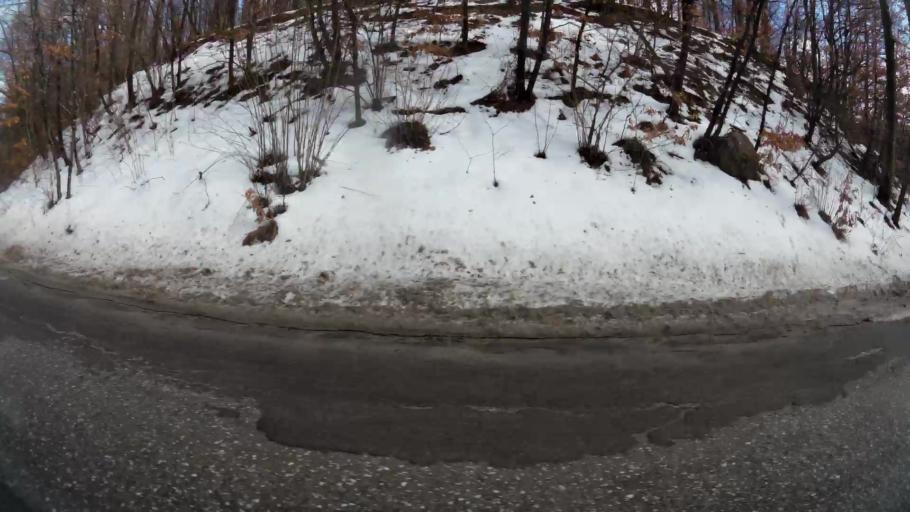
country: BG
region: Sofiya
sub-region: Obshtina Bozhurishte
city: Bozhurishte
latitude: 42.6384
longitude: 23.2174
